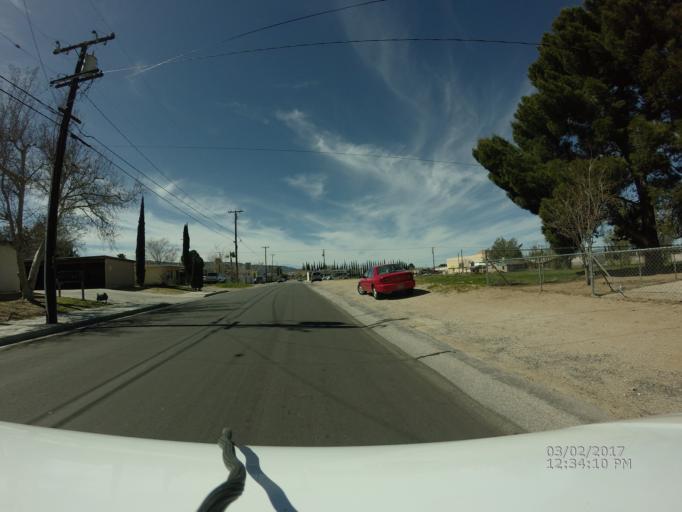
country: US
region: California
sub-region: Los Angeles County
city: Quartz Hill
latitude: 34.6511
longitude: -118.2175
